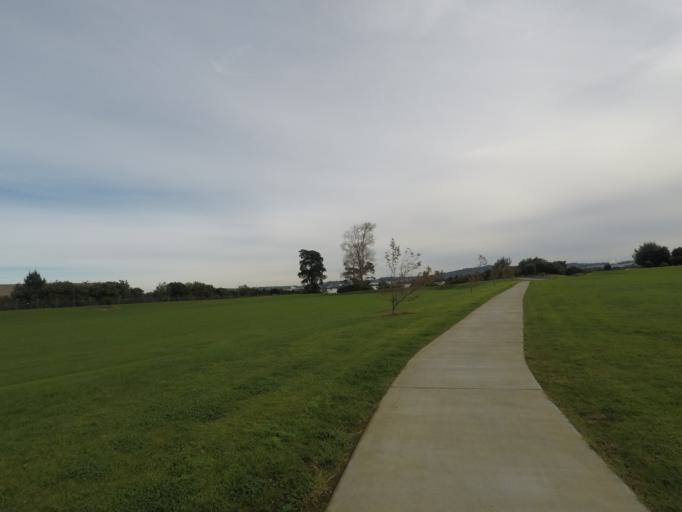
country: NZ
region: Auckland
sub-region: Auckland
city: Mangere
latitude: -36.9455
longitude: 174.8109
